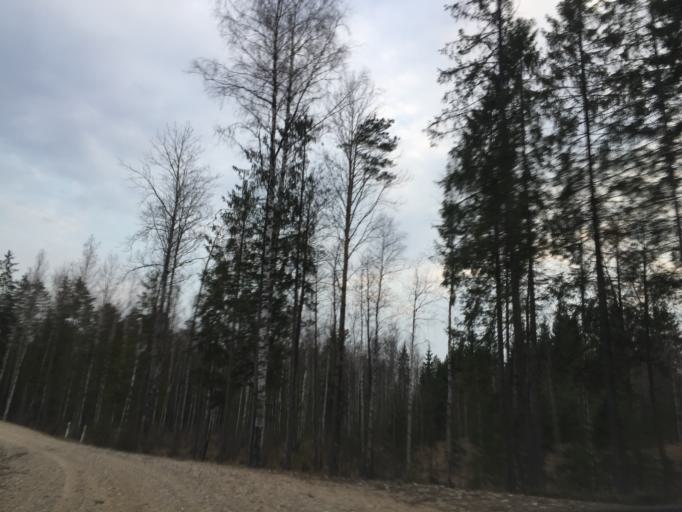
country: LV
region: Raunas
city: Rauna
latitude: 57.1280
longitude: 25.5965
